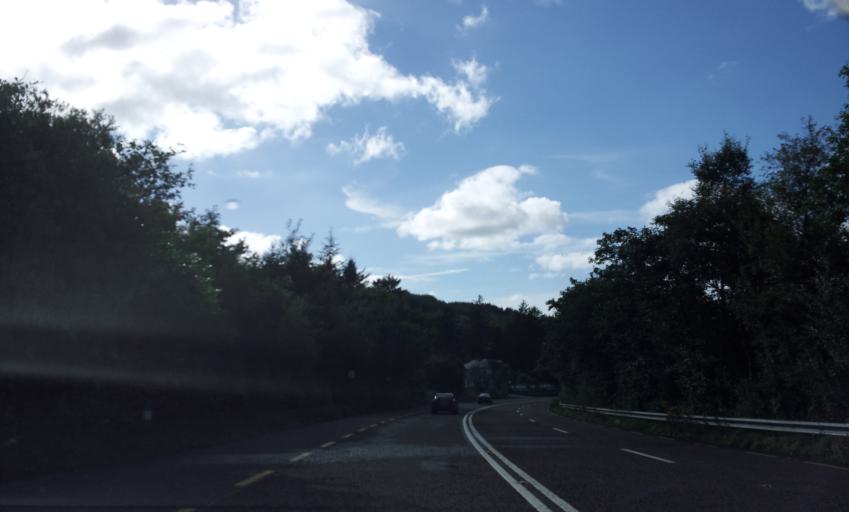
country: IE
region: Munster
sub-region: County Cork
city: Millstreet
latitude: 51.9820
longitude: -9.2750
